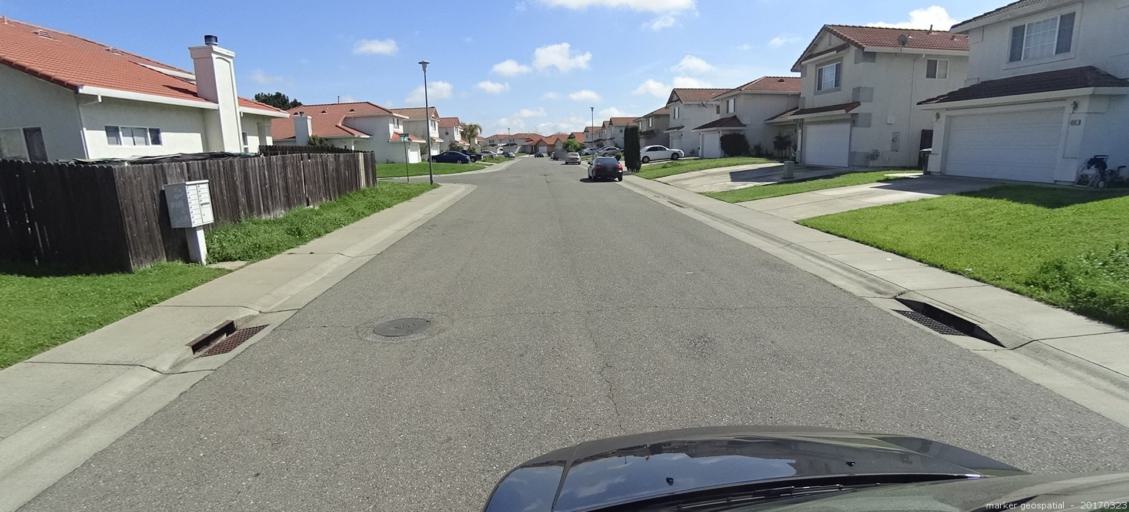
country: US
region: California
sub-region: Sacramento County
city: Florin
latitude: 38.5149
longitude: -121.4213
